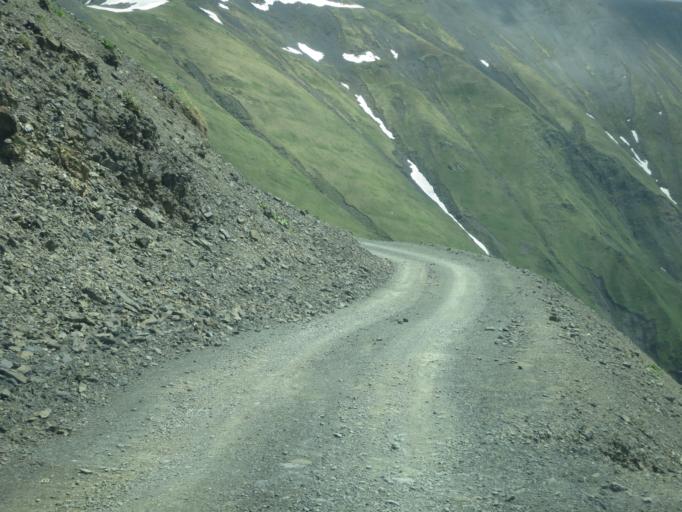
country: GE
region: Kakheti
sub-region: Telavi
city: Telavi
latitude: 42.2743
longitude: 45.4989
